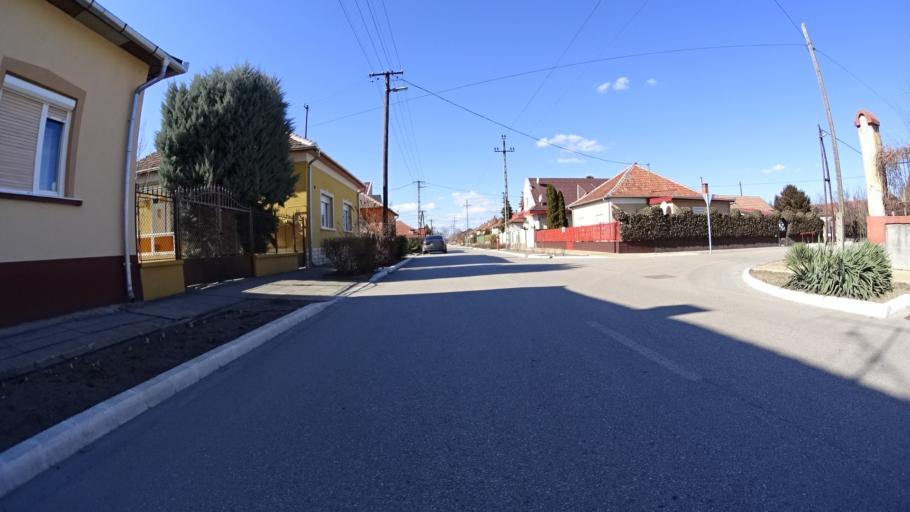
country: HU
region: Bacs-Kiskun
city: Tiszakecske
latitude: 46.9333
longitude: 20.1002
